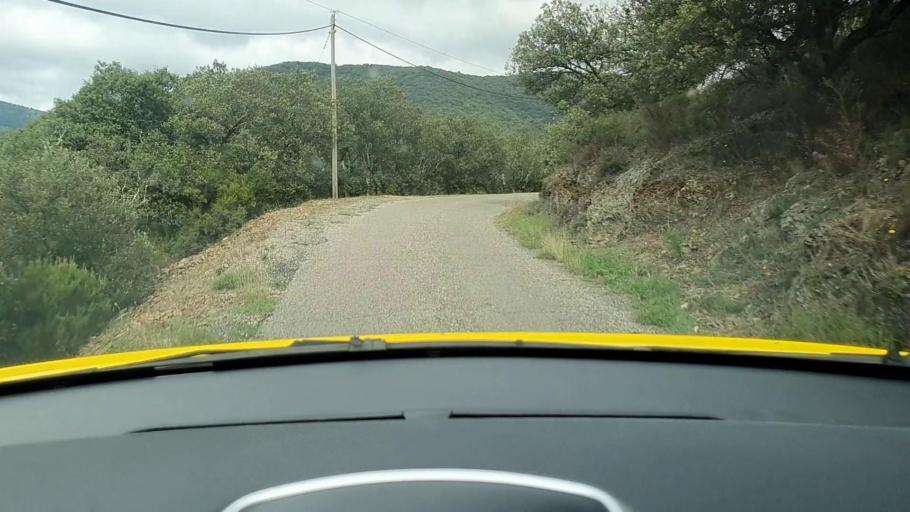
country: FR
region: Languedoc-Roussillon
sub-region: Departement du Gard
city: Sumene
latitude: 44.0161
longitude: 3.6631
